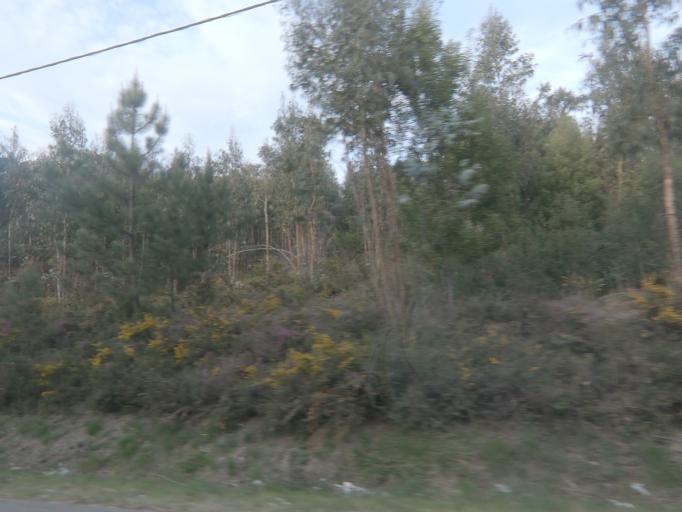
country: PT
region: Porto
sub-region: Valongo
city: Valongo
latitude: 41.1987
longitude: -8.5236
